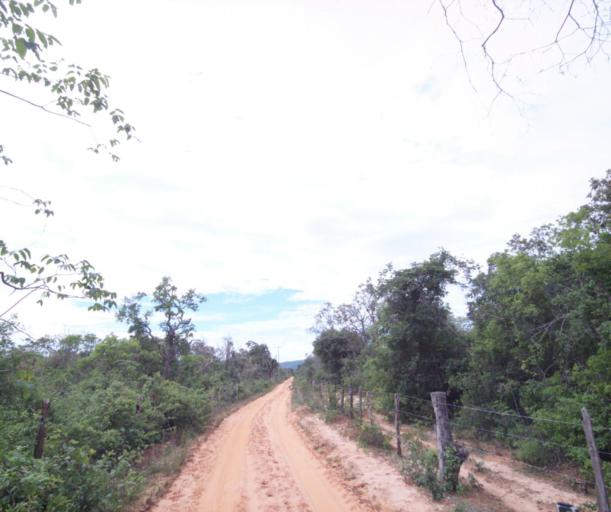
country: BR
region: Bahia
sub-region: Carinhanha
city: Carinhanha
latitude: -14.2381
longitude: -44.3818
